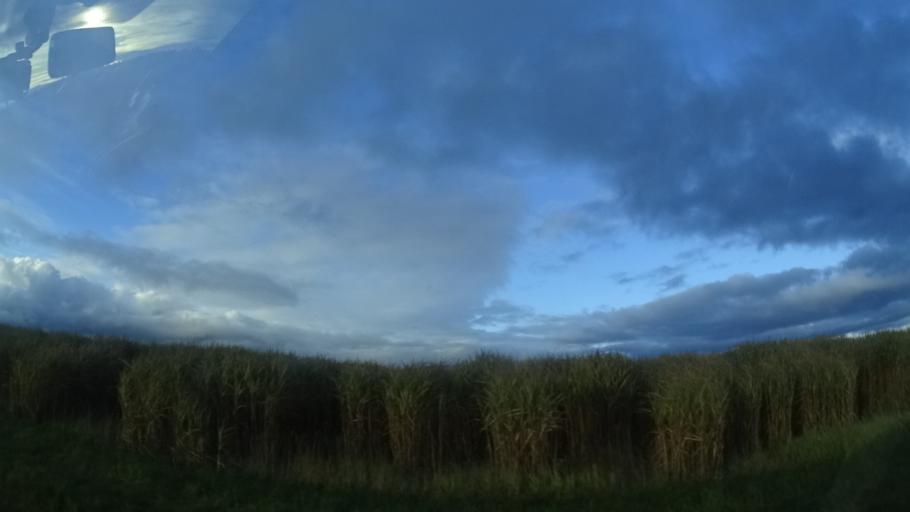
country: DE
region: Hesse
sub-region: Regierungsbezirk Giessen
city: Freiensteinau
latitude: 50.4593
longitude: 9.4146
